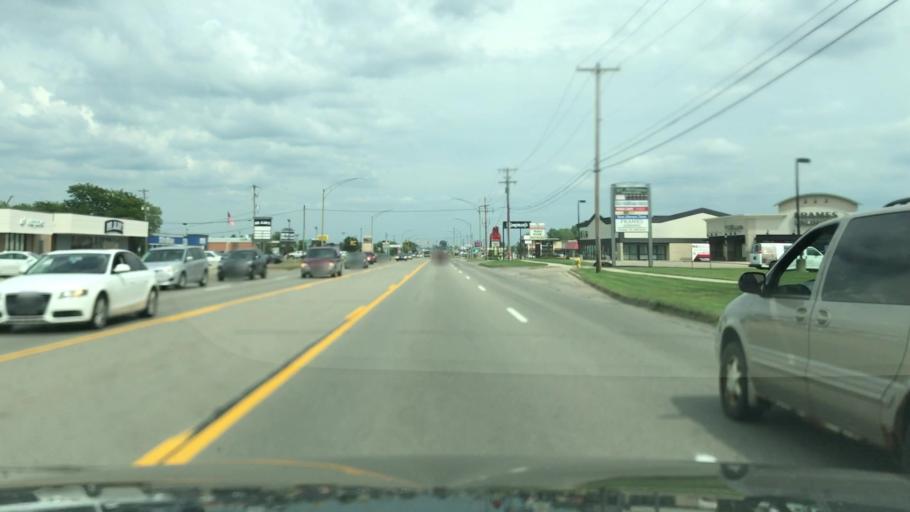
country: US
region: Michigan
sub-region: Kent County
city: East Grand Rapids
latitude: 42.9125
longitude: -85.5958
